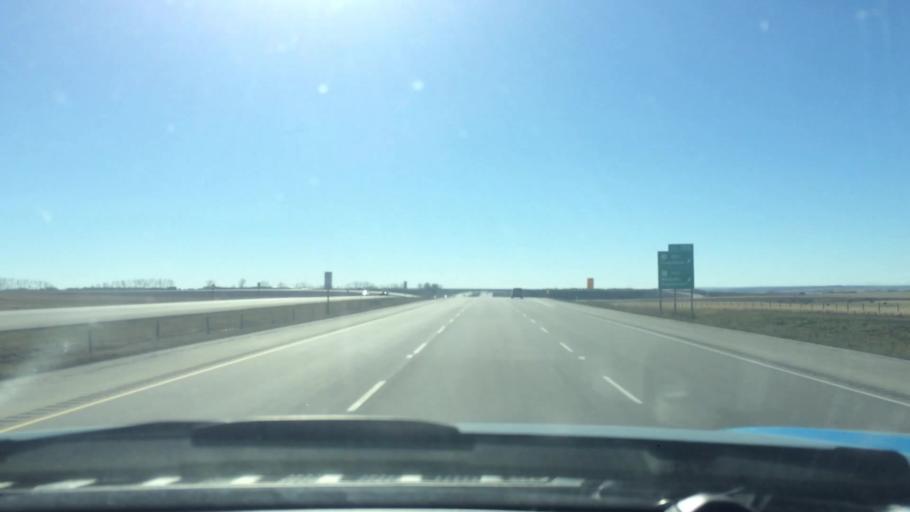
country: CA
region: Alberta
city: Crossfield
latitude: 51.3948
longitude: -114.0021
